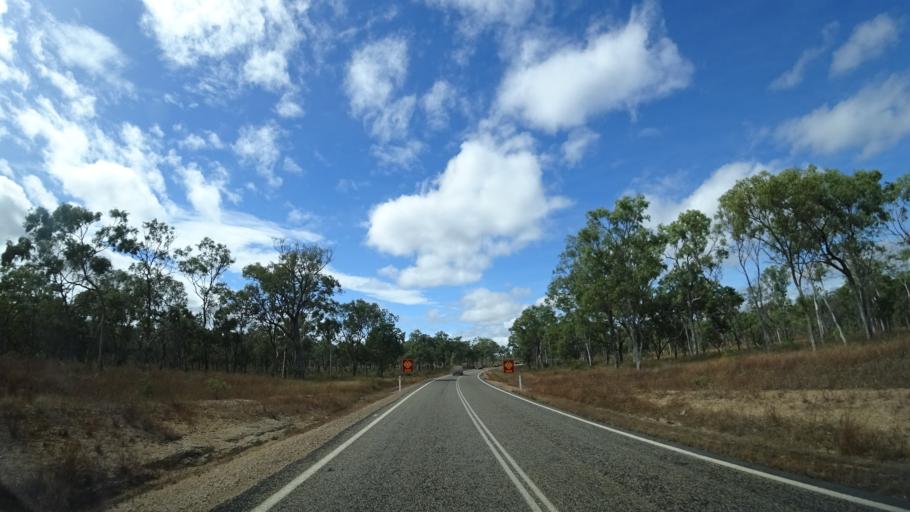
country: AU
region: Queensland
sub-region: Cairns
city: Port Douglas
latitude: -16.4970
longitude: 144.9982
